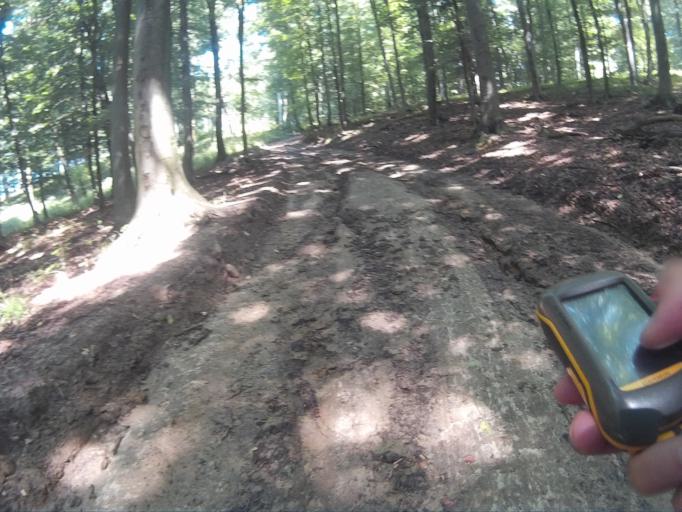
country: HU
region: Veszprem
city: Zirc
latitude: 47.1867
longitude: 17.8756
